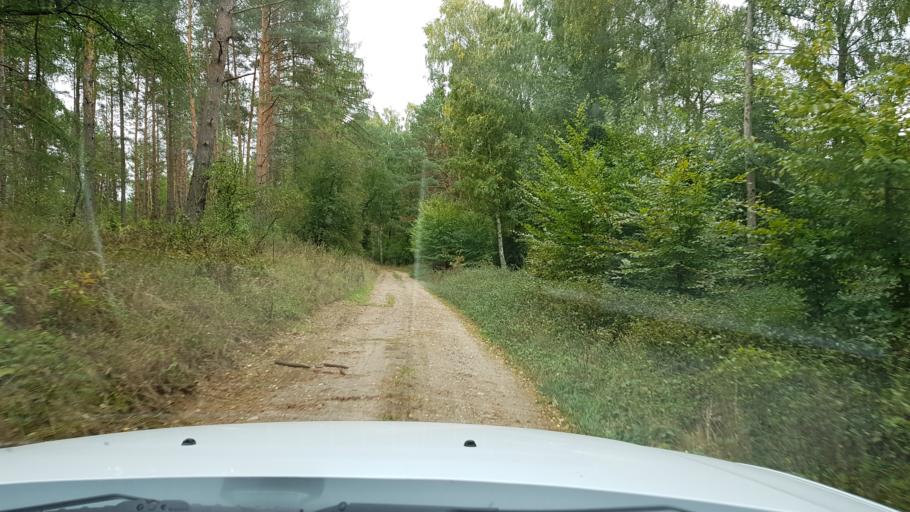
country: PL
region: West Pomeranian Voivodeship
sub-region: Powiat gryfinski
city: Cedynia
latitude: 52.8386
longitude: 14.2777
